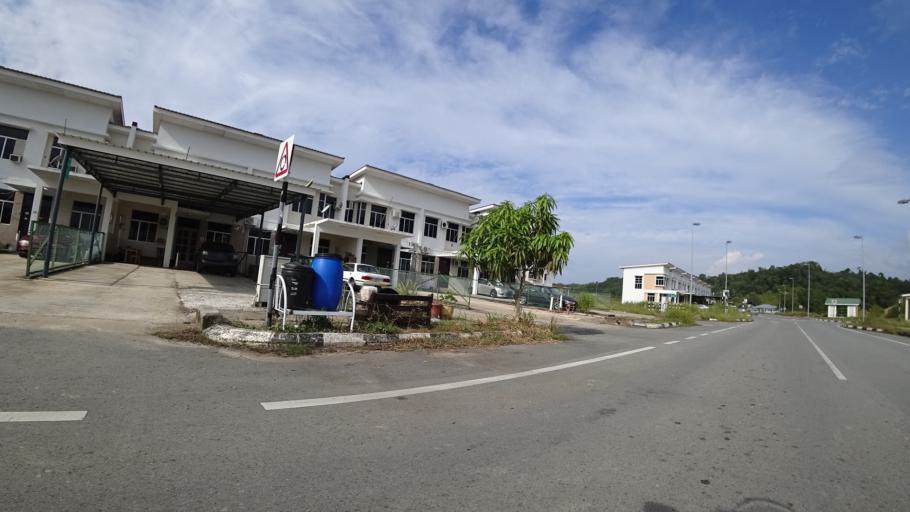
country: BN
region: Brunei and Muara
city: Bandar Seri Begawan
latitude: 4.8870
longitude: 114.7989
